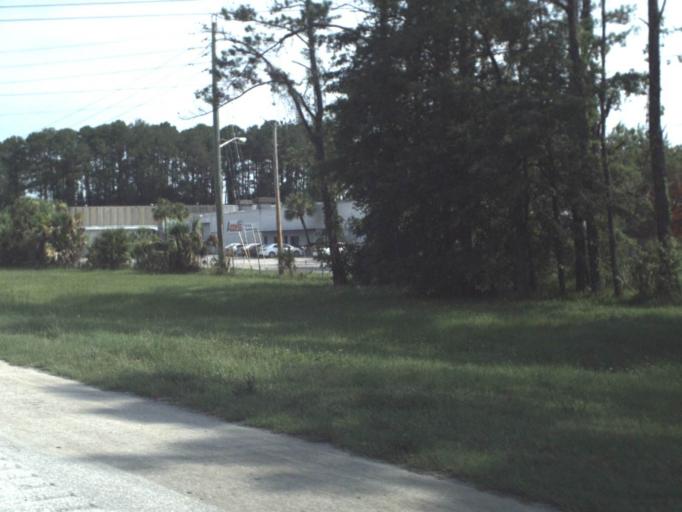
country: US
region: Florida
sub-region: Duval County
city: Jacksonville
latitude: 30.2346
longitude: -81.5800
